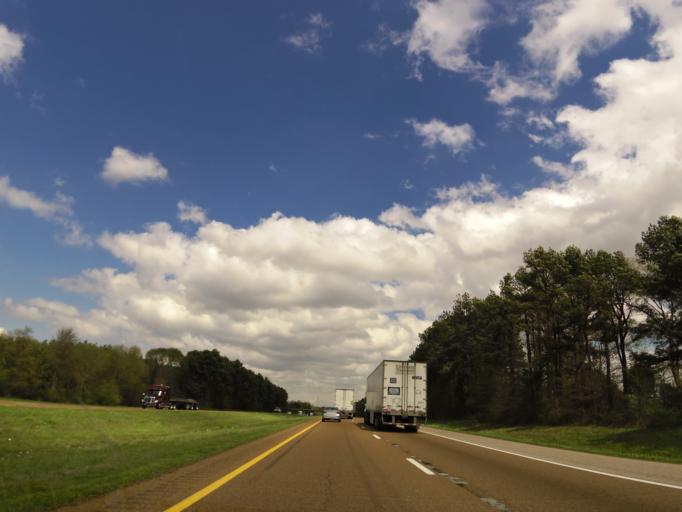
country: US
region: Tennessee
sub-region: Tipton County
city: Mason
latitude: 35.3612
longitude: -89.4913
